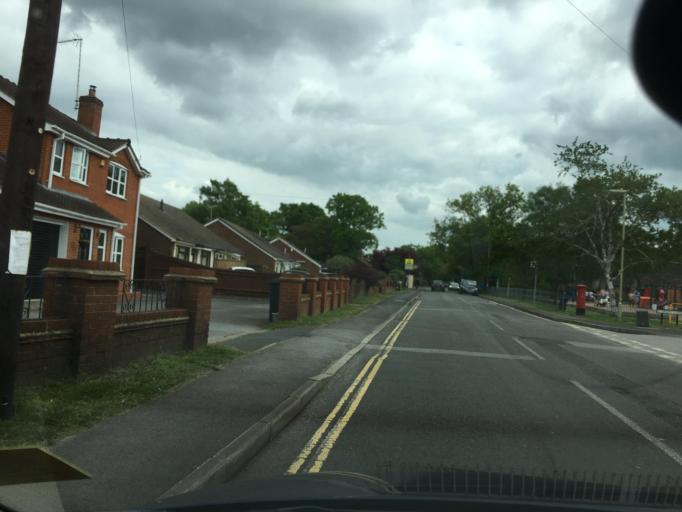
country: GB
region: England
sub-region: Bracknell Forest
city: Sandhurst
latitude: 51.3344
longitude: -0.7950
